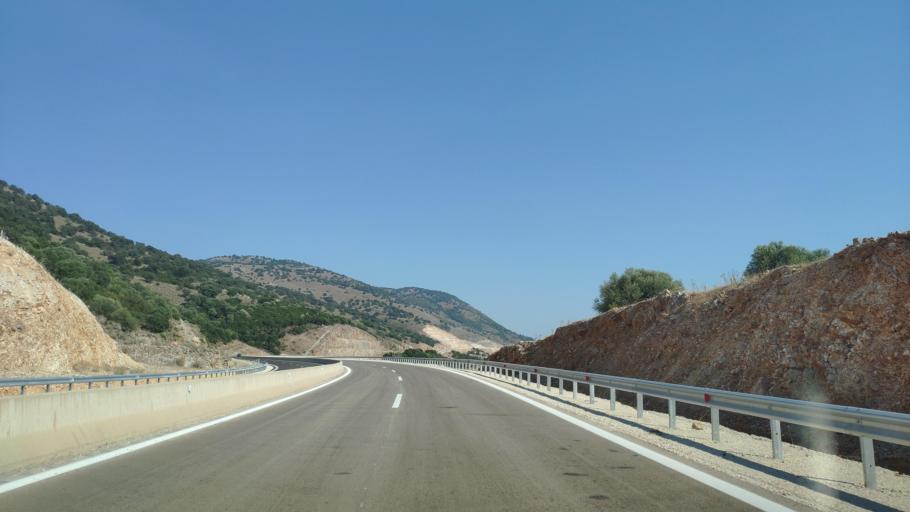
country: GR
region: West Greece
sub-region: Nomos Aitolias kai Akarnanias
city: Katouna
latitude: 38.8394
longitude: 21.1109
